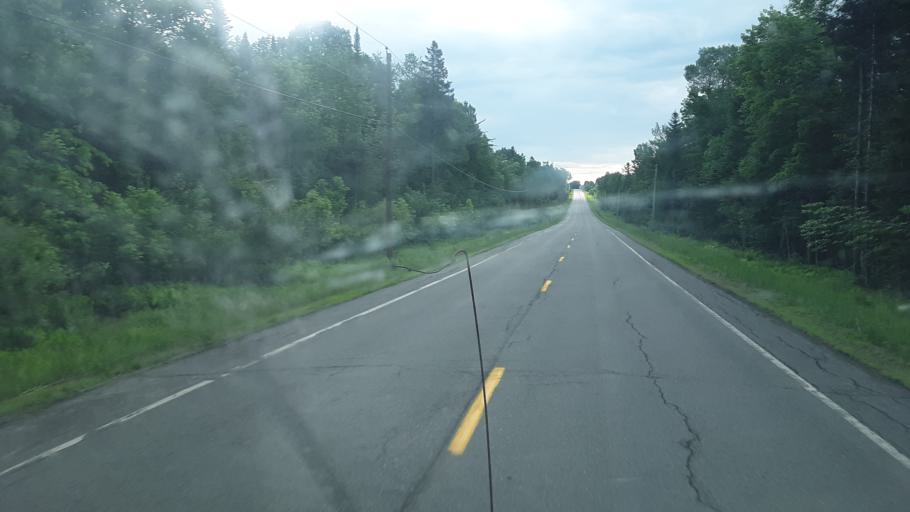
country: US
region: Maine
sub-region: Penobscot County
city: Patten
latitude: 45.8709
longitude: -68.3425
